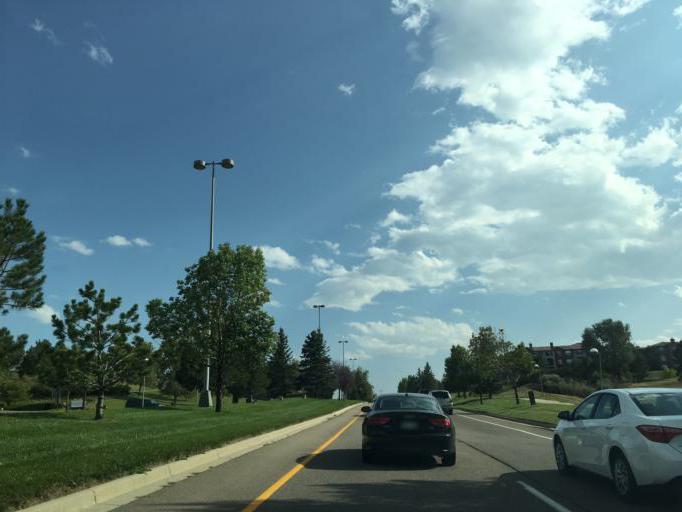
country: US
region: Colorado
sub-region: Broomfield County
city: Broomfield
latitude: 39.9274
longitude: -105.1279
